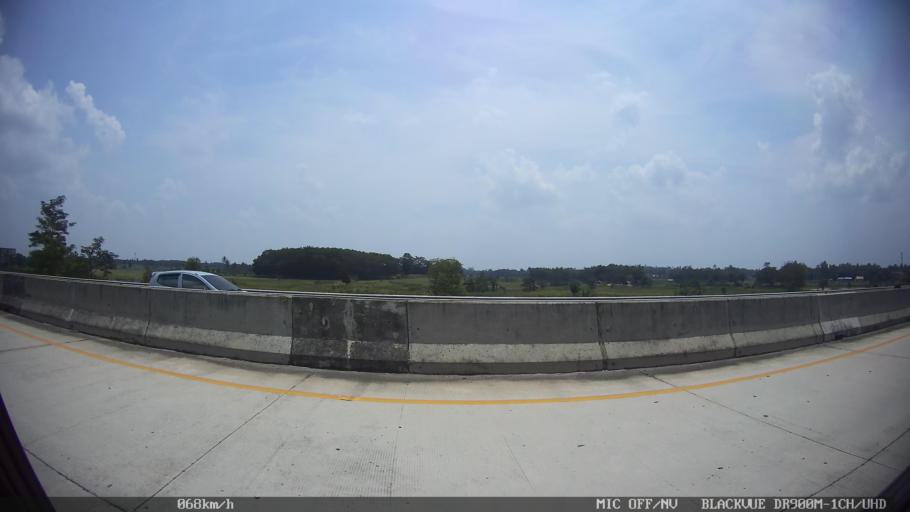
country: ID
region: Lampung
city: Natar
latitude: -5.2857
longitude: 105.2205
